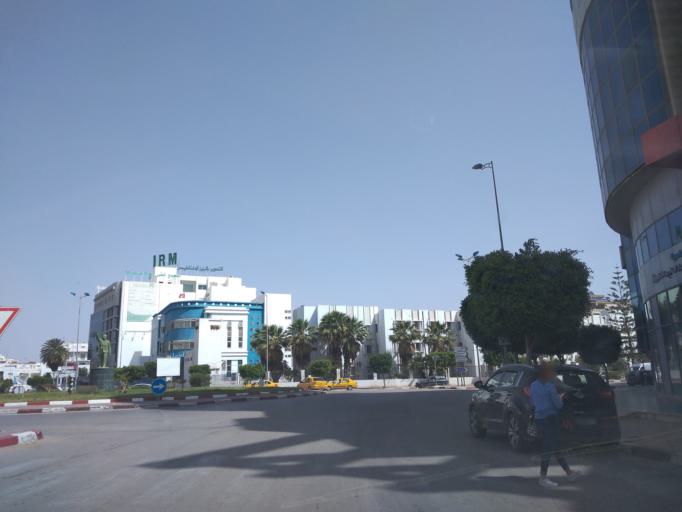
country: TN
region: Safaqis
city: Sfax
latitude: 34.7409
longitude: 10.7527
